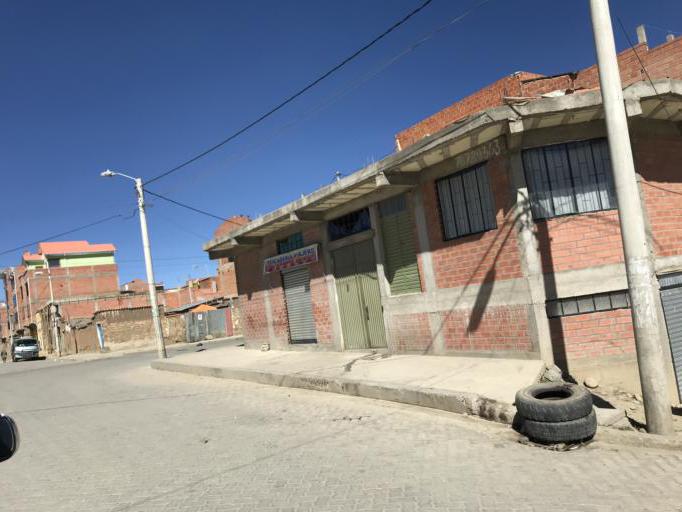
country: BO
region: La Paz
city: La Paz
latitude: -16.4863
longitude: -68.2008
